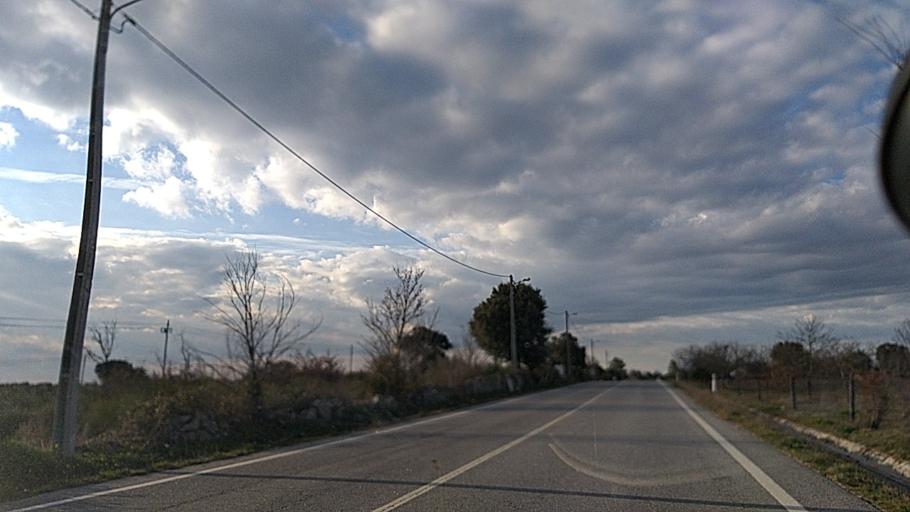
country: ES
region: Castille and Leon
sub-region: Provincia de Salamanca
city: Aldea del Obispo
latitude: 40.6908
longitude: -6.8784
